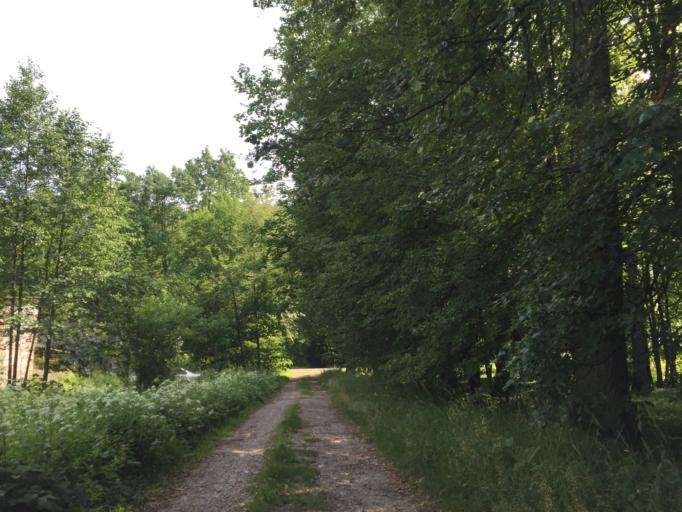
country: LV
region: Jelgava
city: Jelgava
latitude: 56.6847
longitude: 23.7212
